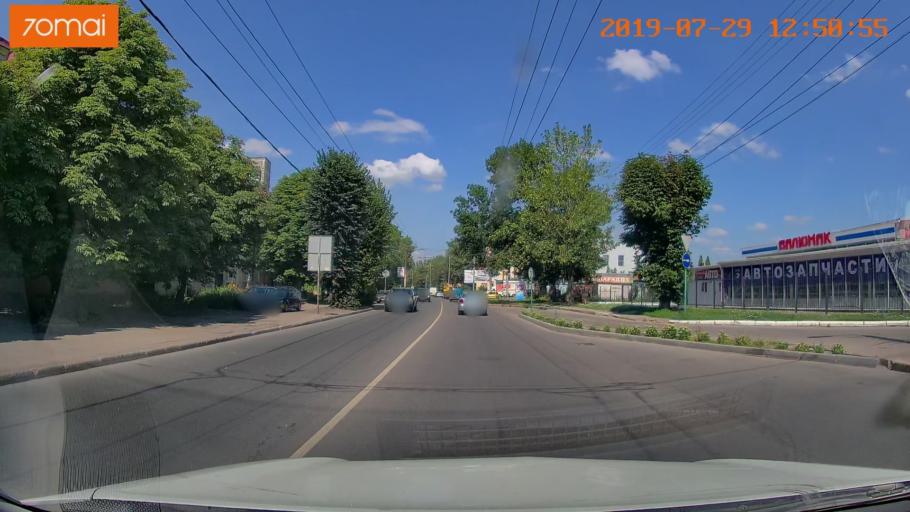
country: RU
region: Kaliningrad
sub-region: Gorod Kaliningrad
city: Kaliningrad
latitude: 54.6900
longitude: 20.5312
